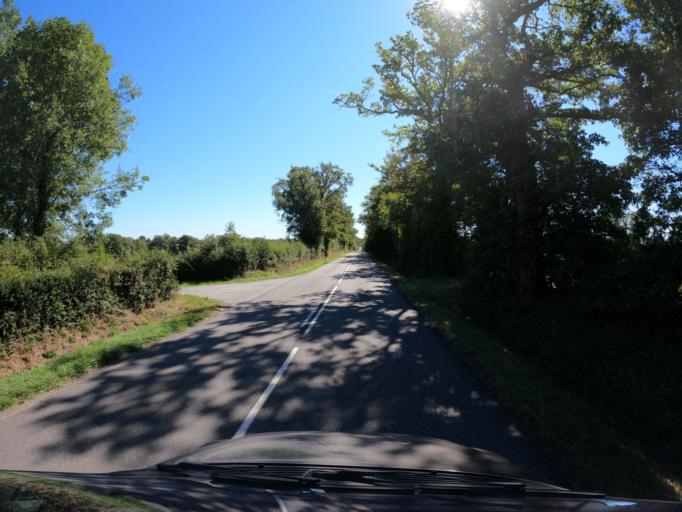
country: FR
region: Limousin
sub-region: Departement de la Haute-Vienne
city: Le Dorat
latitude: 46.2627
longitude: 1.0339
